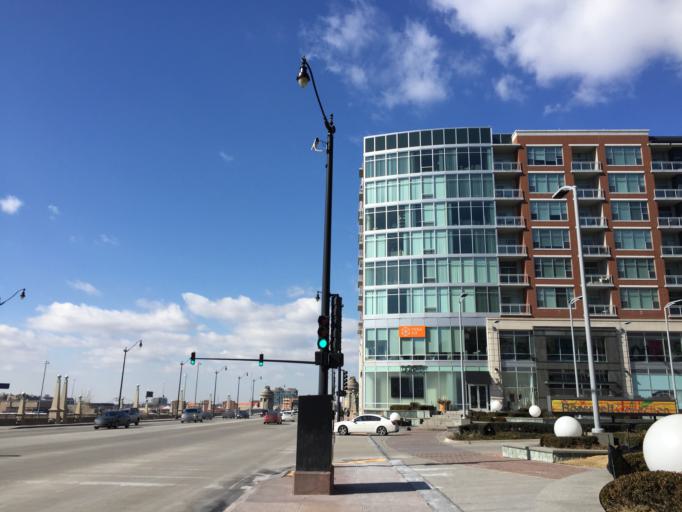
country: US
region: Illinois
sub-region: Cook County
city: Chicago
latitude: 41.8675
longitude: -87.6321
